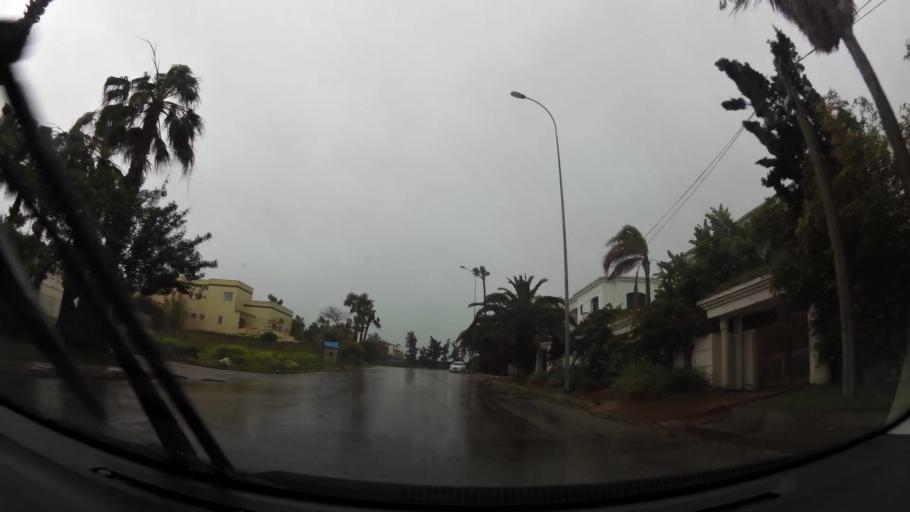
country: MA
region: Grand Casablanca
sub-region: Casablanca
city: Casablanca
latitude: 33.5847
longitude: -7.6767
